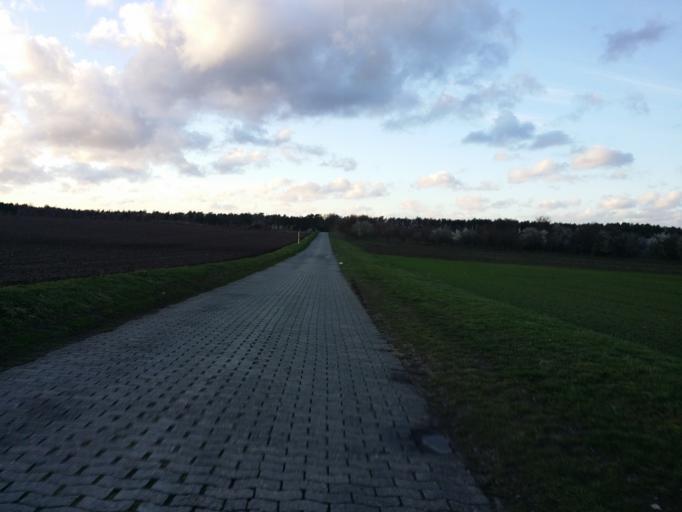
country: DE
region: Lower Saxony
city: Gross Ippener
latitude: 52.9610
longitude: 8.6038
